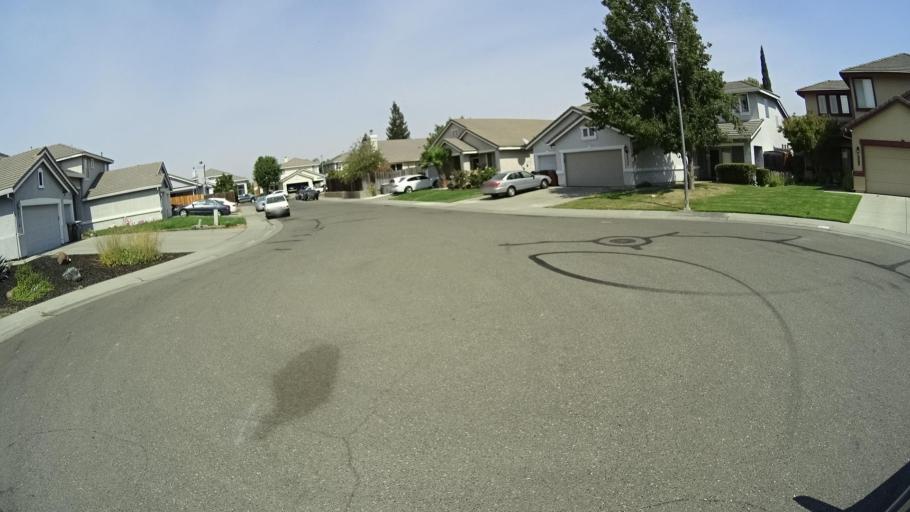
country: US
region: California
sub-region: Sacramento County
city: Vineyard
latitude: 38.4476
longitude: -121.3759
